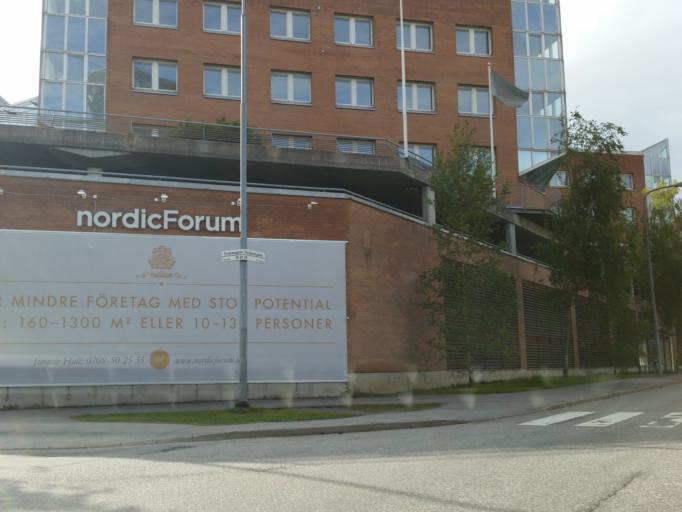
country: SE
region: Stockholm
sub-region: Stockholms Kommun
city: Kista
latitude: 59.4069
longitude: 17.9534
